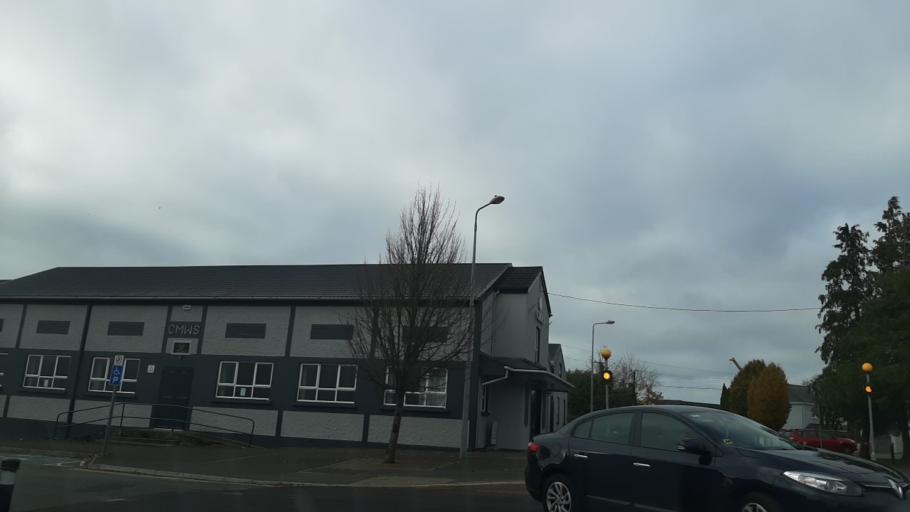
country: IE
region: Leinster
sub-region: Kildare
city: Kildare
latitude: 53.1552
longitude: -6.9117
